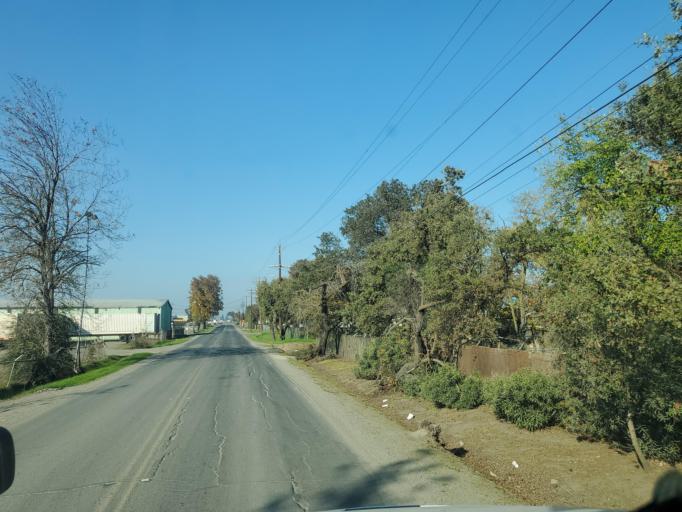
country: US
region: California
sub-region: San Joaquin County
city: August
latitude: 37.9719
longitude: -121.2486
